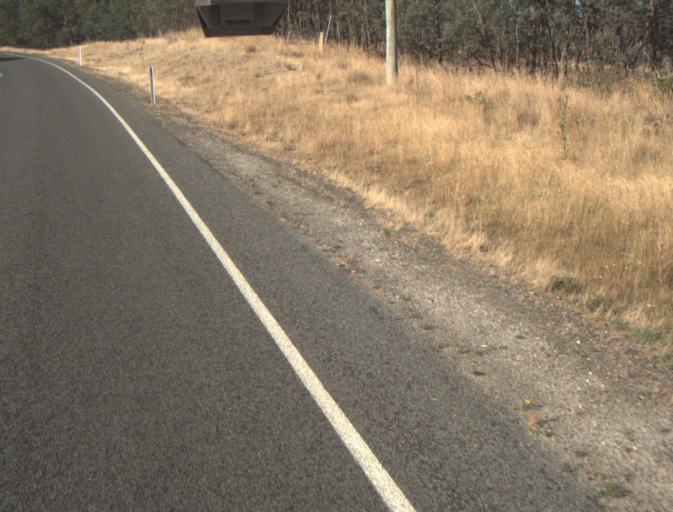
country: AU
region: Tasmania
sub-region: Launceston
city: Newstead
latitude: -41.4322
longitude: 147.2517
